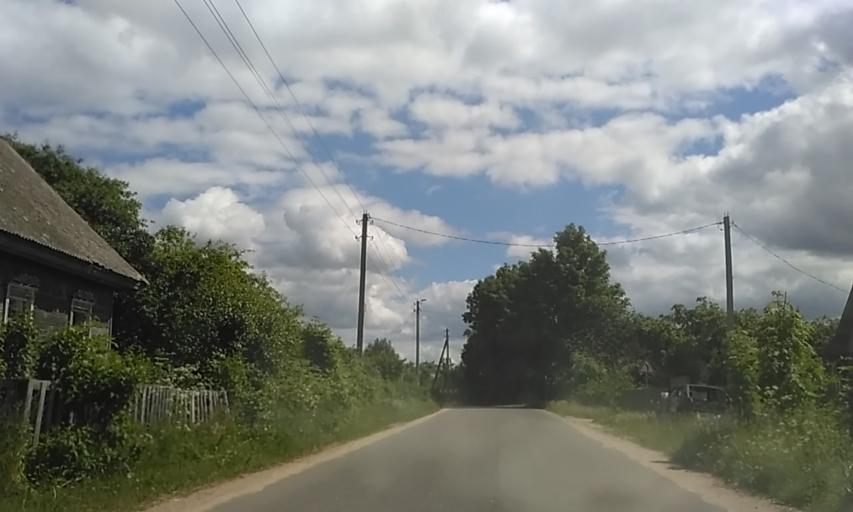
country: BY
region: Minsk
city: Krupki
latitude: 54.3520
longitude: 29.1156
